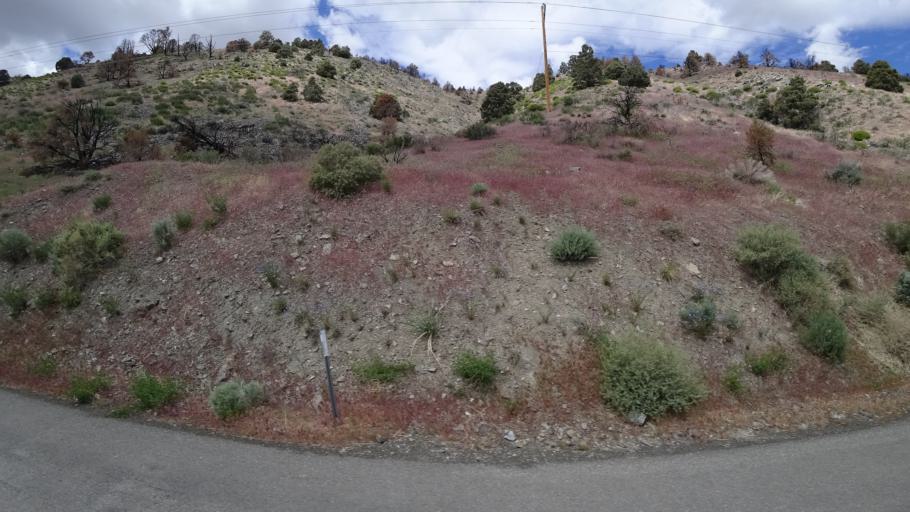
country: US
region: Nevada
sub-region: Lyon County
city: Smith Valley
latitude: 38.6739
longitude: -119.5490
